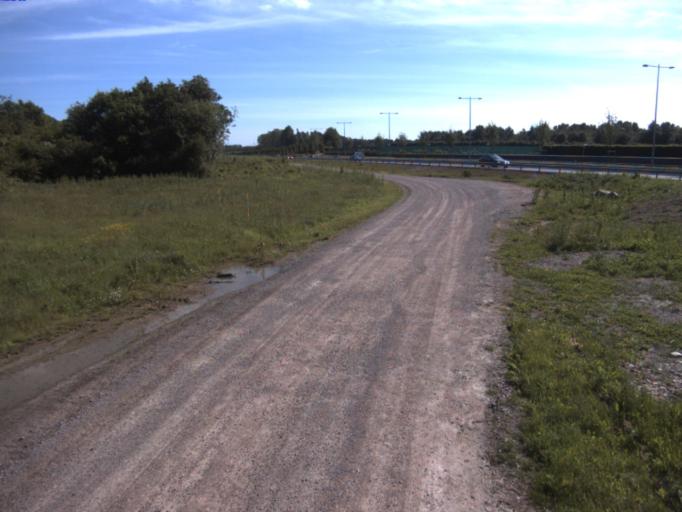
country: SE
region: Skane
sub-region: Helsingborg
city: Odakra
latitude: 56.0602
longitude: 12.7489
